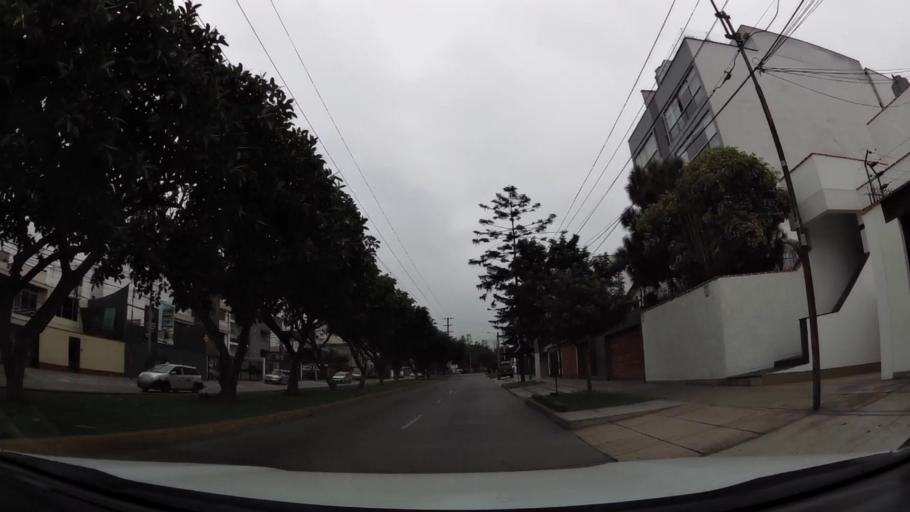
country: PE
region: Lima
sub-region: Lima
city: Surco
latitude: -12.1258
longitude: -77.0092
